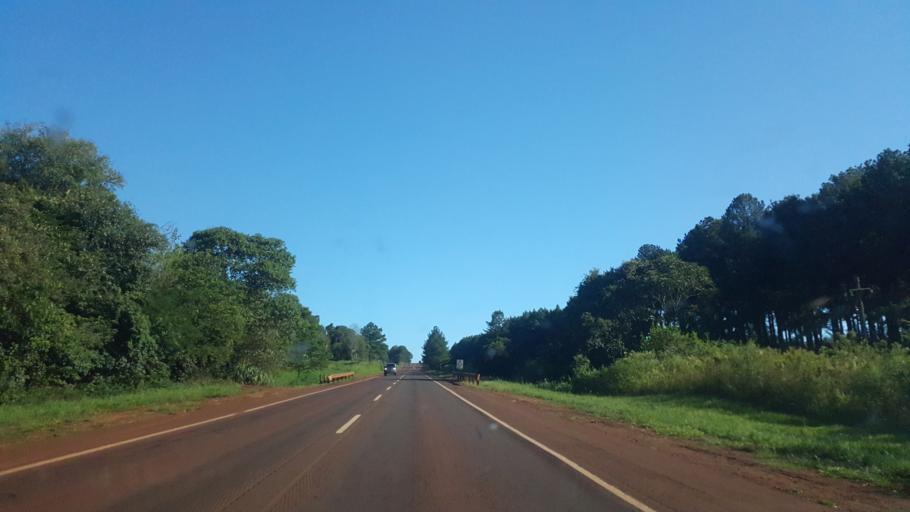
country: AR
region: Misiones
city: Puerto Esperanza
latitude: -26.1527
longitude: -54.5830
